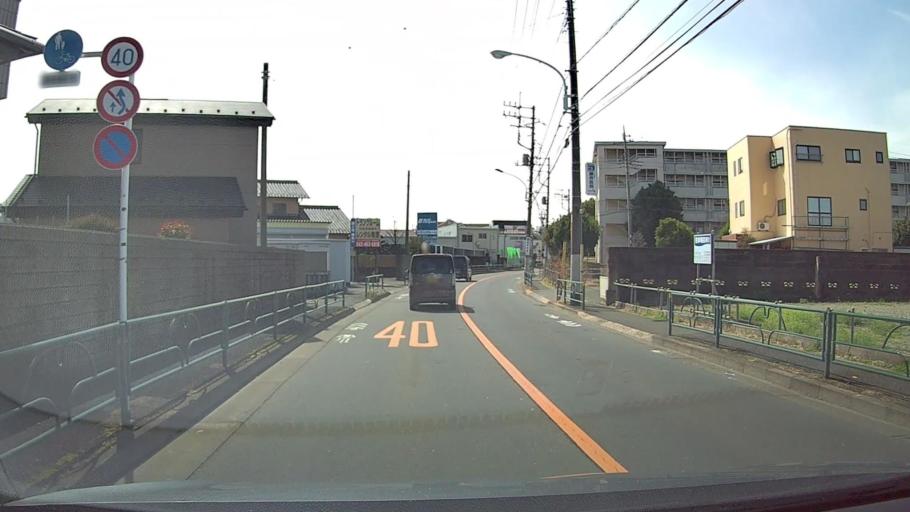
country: JP
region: Tokyo
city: Tanashicho
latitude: 35.7532
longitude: 139.5515
